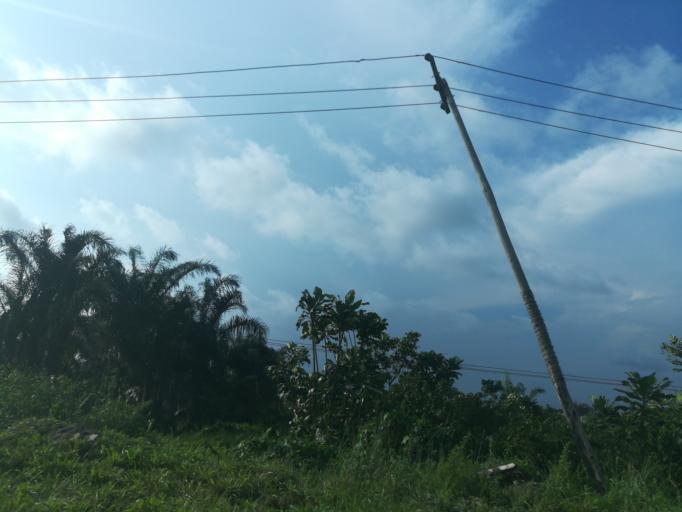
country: NG
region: Ogun
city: Ado Odo
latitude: 6.4930
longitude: 3.0804
